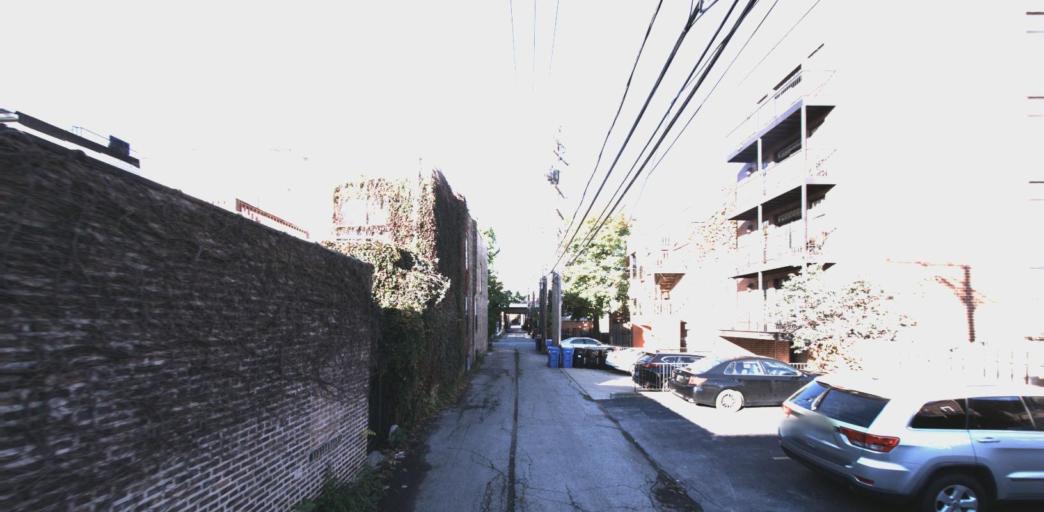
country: US
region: Illinois
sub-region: Cook County
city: Chicago
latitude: 41.9322
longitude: -87.6521
